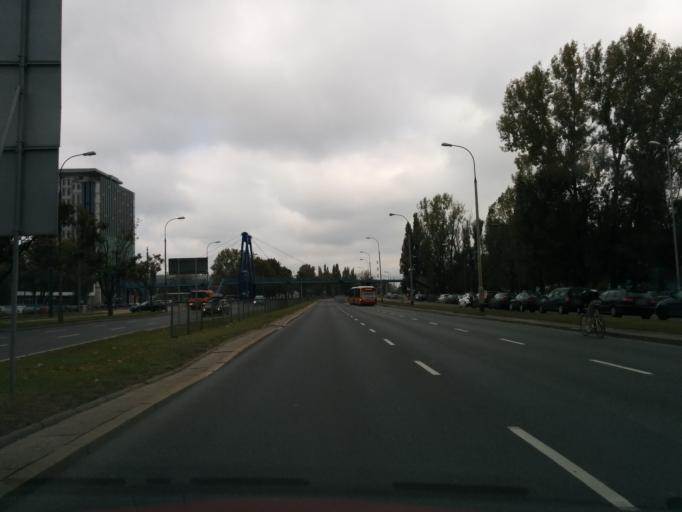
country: PL
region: Masovian Voivodeship
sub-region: Warszawa
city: Praga Polnoc
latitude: 52.2693
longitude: 21.0188
